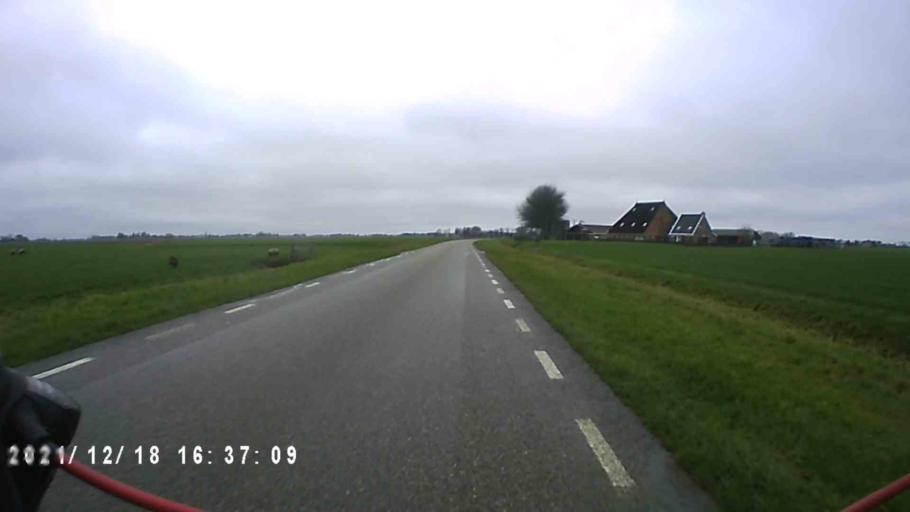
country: NL
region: Friesland
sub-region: Gemeente Dongeradeel
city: Dokkum
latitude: 53.3578
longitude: 6.0173
